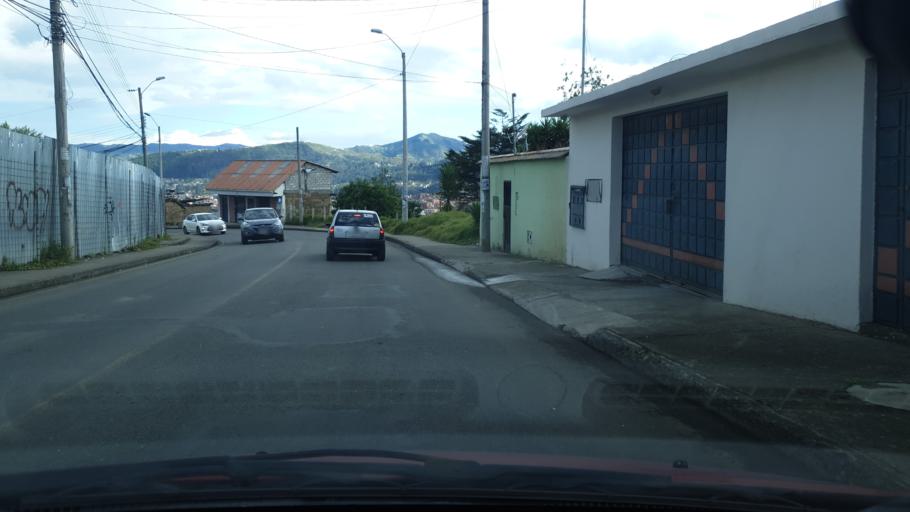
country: EC
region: Azuay
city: Cuenca
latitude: -2.8871
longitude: -79.0151
